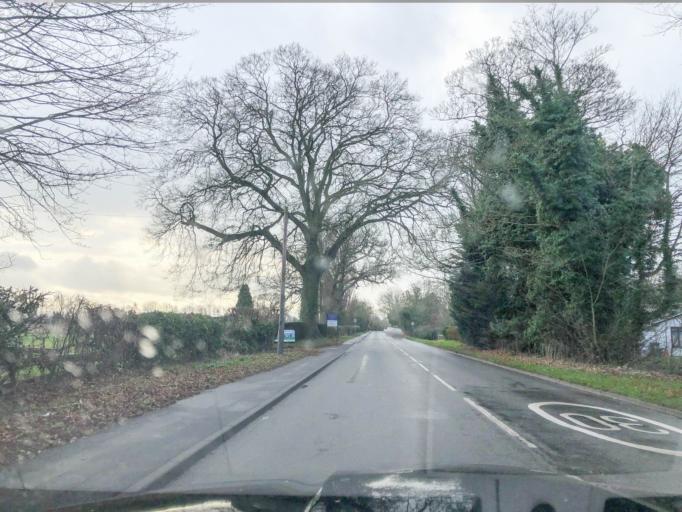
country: GB
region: England
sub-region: Warwickshire
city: Kenilworth
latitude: 52.3316
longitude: -1.5737
